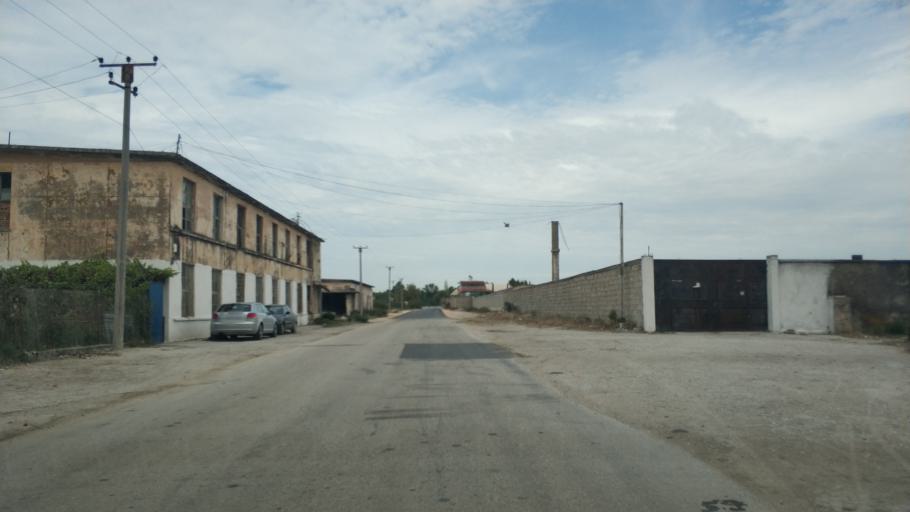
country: AL
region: Vlore
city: Vlore
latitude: 40.4741
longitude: 19.4556
